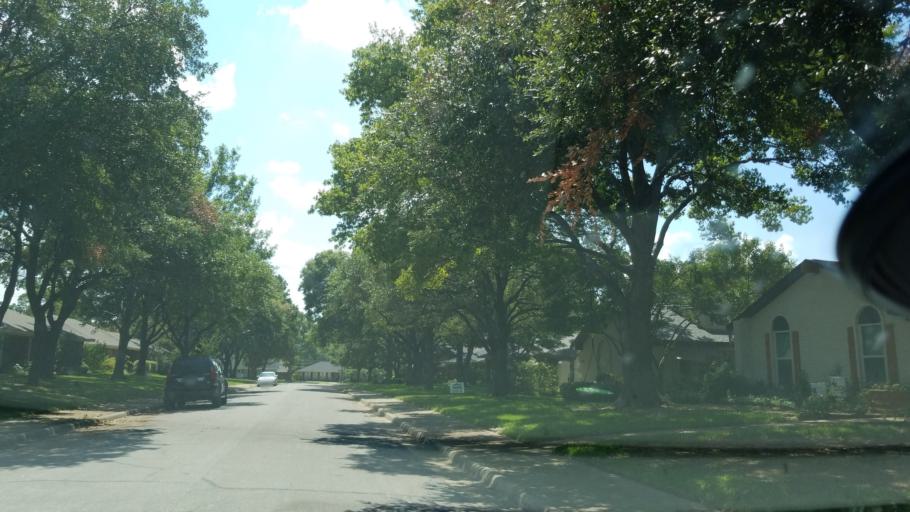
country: US
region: Texas
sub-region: Dallas County
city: Richardson
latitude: 32.8911
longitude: -96.7120
